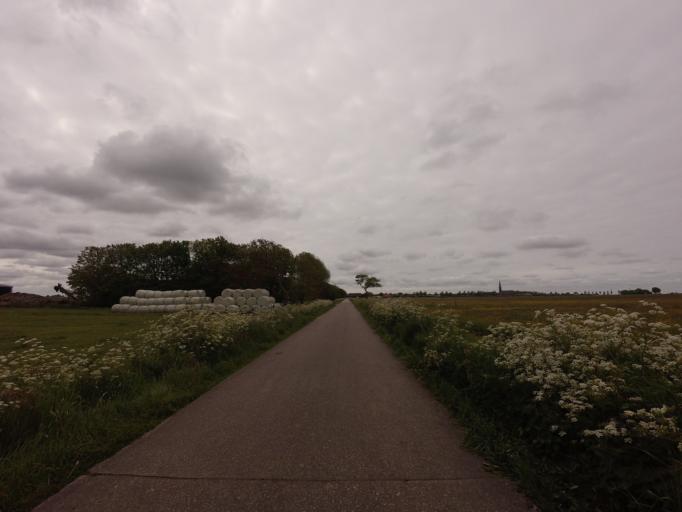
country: NL
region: Friesland
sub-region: Sudwest Fryslan
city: Workum
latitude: 52.9911
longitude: 5.4580
